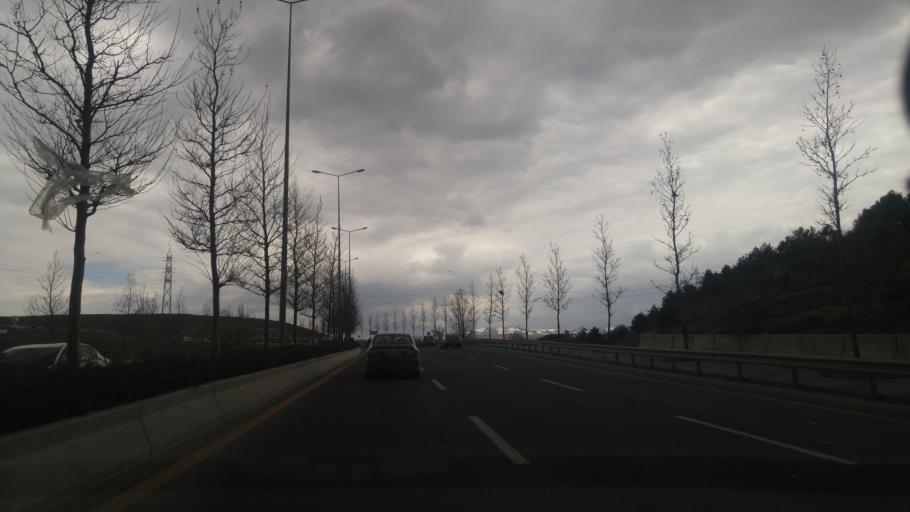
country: TR
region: Ankara
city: Mamak
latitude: 39.8863
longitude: 32.9148
